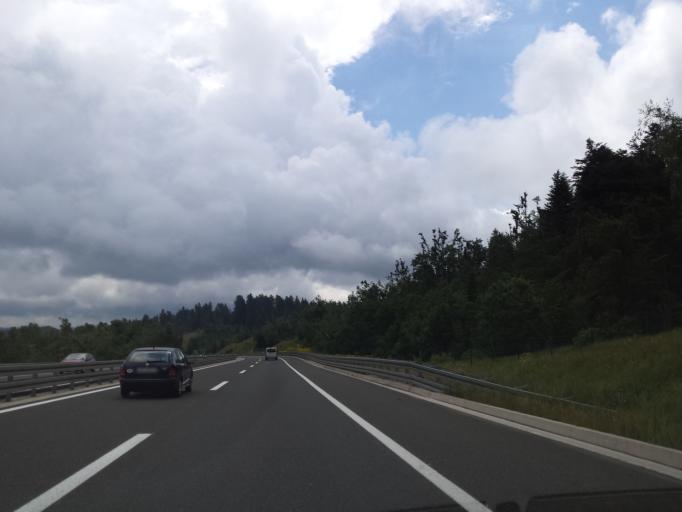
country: HR
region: Primorsko-Goranska
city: Hreljin
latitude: 45.3187
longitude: 14.6733
